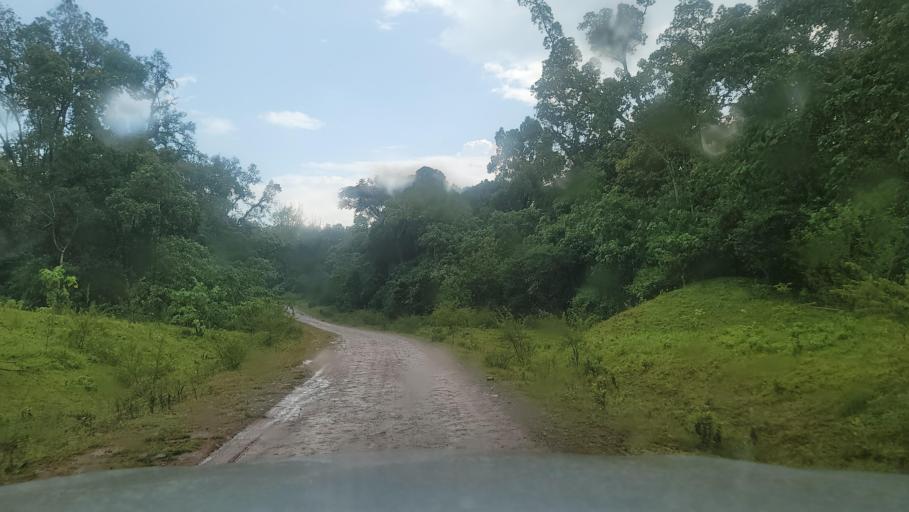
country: ET
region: Southern Nations, Nationalities, and People's Region
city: Bonga
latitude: 7.6672
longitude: 36.2429
